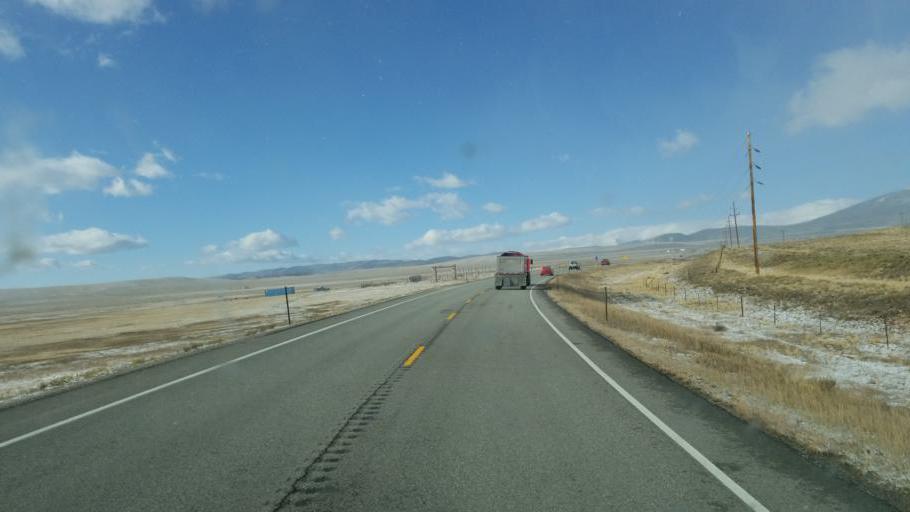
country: US
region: Colorado
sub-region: Park County
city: Fairplay
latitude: 39.3572
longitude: -105.8192
